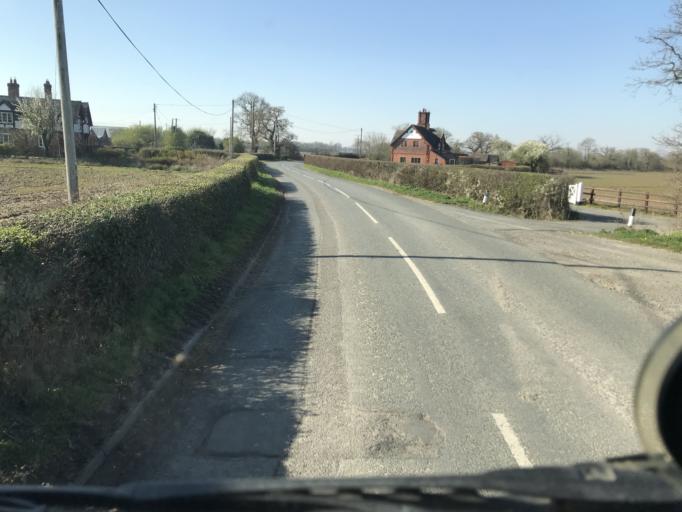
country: GB
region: England
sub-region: Cheshire West and Chester
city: Aldford
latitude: 53.1355
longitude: -2.8458
